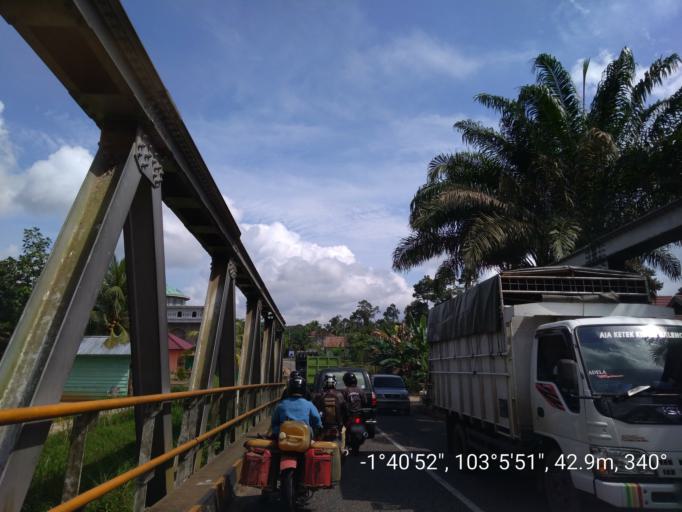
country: ID
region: Jambi
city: Muara Tembesi
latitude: -1.6821
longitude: 103.0987
